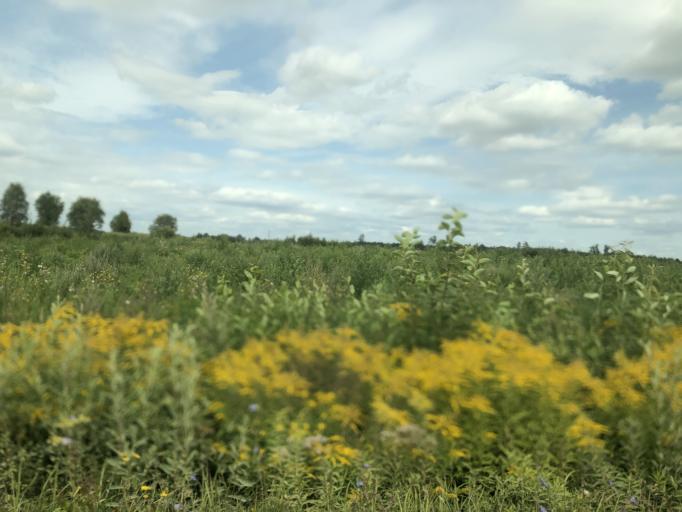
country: LV
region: Vecumnieki
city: Vecumnieki
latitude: 56.4612
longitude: 24.6221
